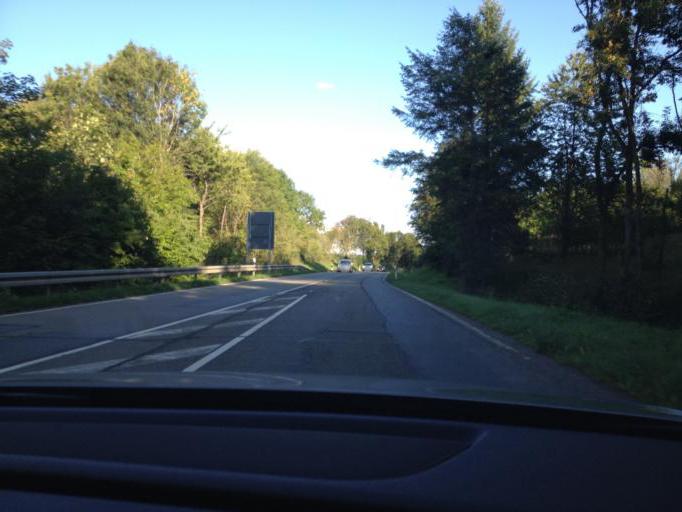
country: DE
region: Saarland
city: Tholey
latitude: 49.4941
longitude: 7.0383
